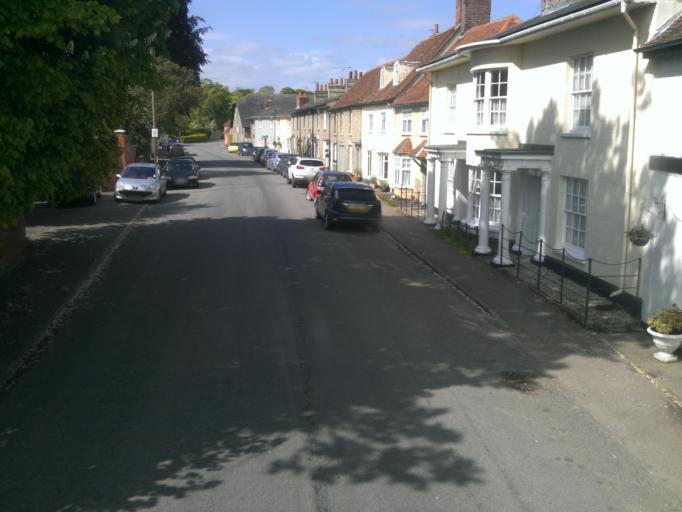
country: GB
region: England
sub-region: Suffolk
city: East Bergholt
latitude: 51.9655
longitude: 0.9720
